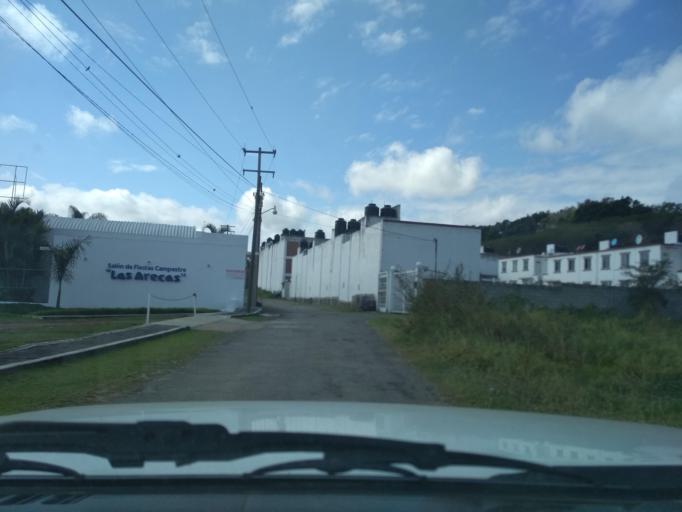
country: MX
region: Veracruz
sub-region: Emiliano Zapata
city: Dos Rios
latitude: 19.4836
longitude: -96.8105
